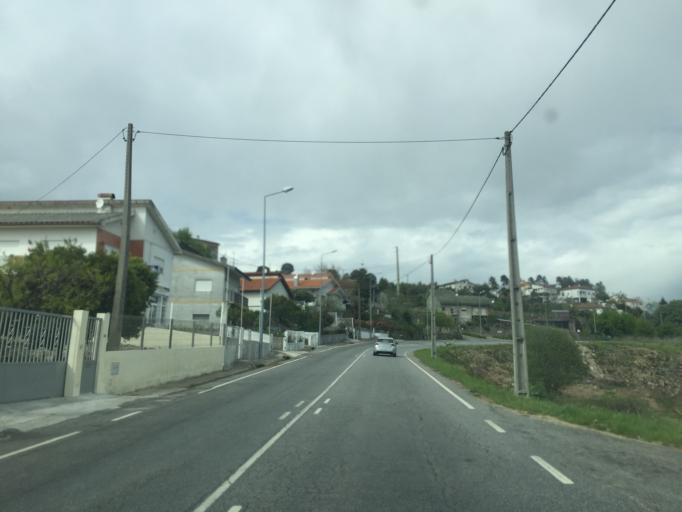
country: PT
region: Viseu
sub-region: Viseu
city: Viseu
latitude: 40.6556
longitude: -7.9391
